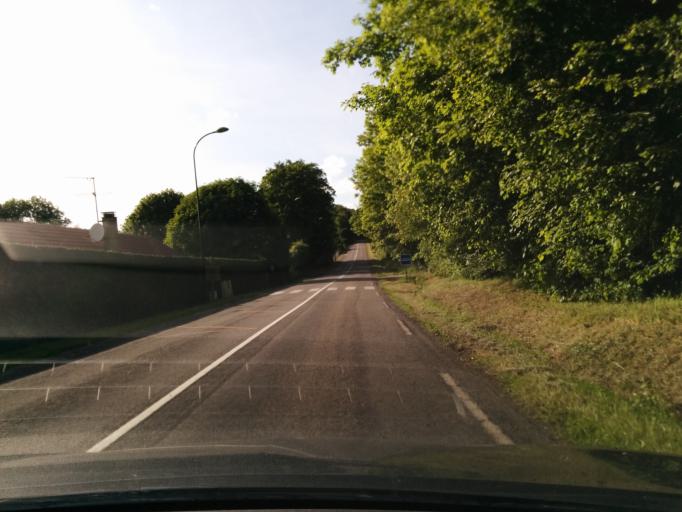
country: FR
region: Haute-Normandie
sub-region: Departement de l'Eure
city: Saint-Marcel
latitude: 49.1177
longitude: 1.4617
